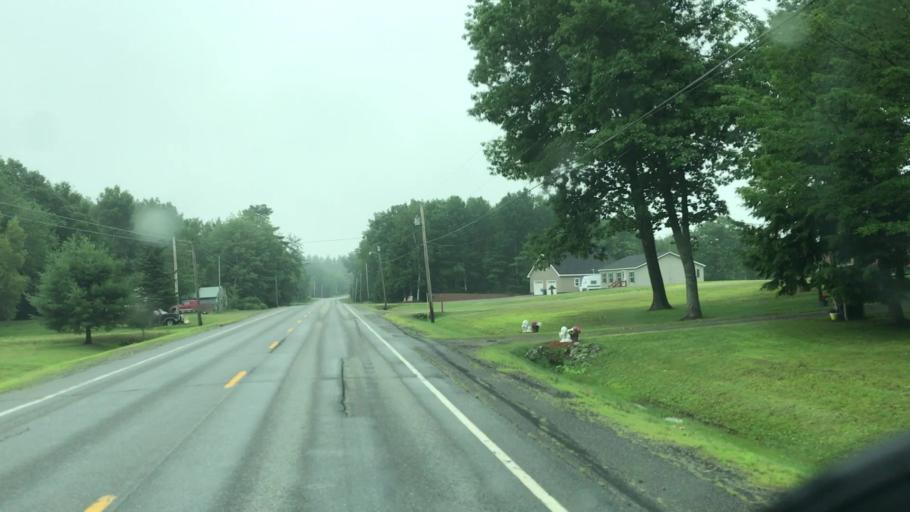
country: US
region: Maine
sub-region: Penobscot County
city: Howland
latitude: 45.2586
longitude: -68.6379
